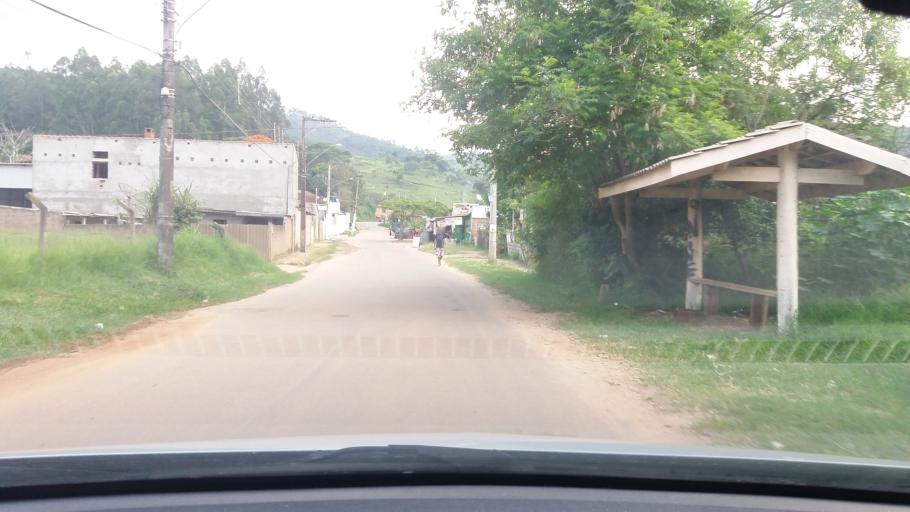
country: BR
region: Sao Paulo
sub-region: Bom Jesus Dos Perdoes
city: Bom Jesus dos Perdoes
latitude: -23.1700
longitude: -46.4795
